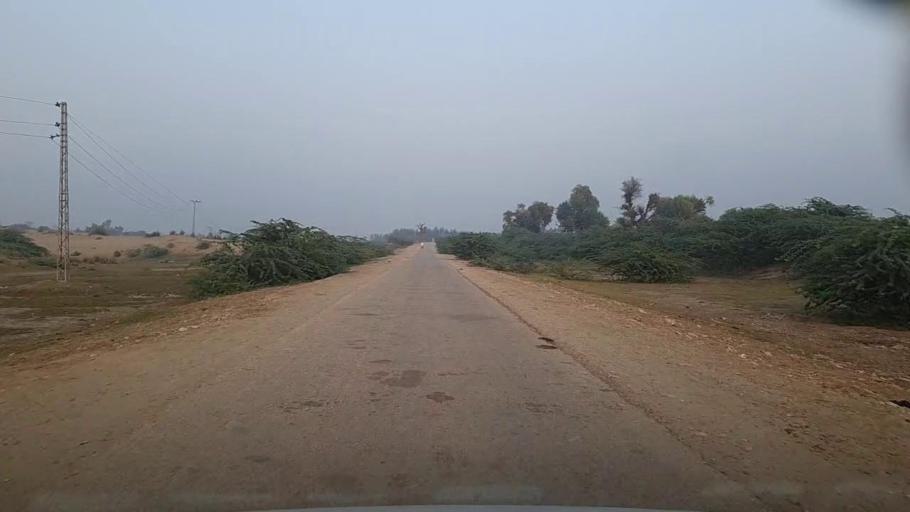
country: PK
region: Sindh
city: Bozdar
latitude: 27.0442
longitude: 68.5915
